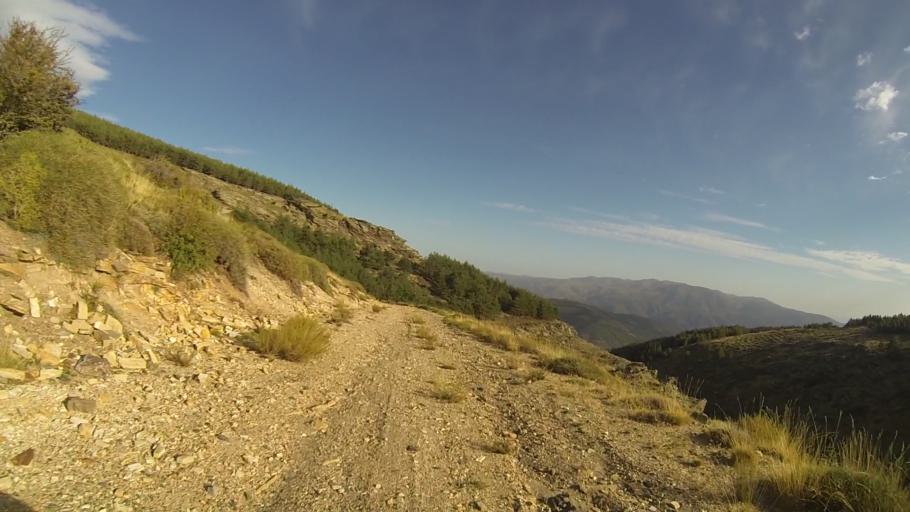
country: ES
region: Andalusia
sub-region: Provincia de Almeria
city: Paterna del Rio
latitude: 37.0744
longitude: -2.8964
